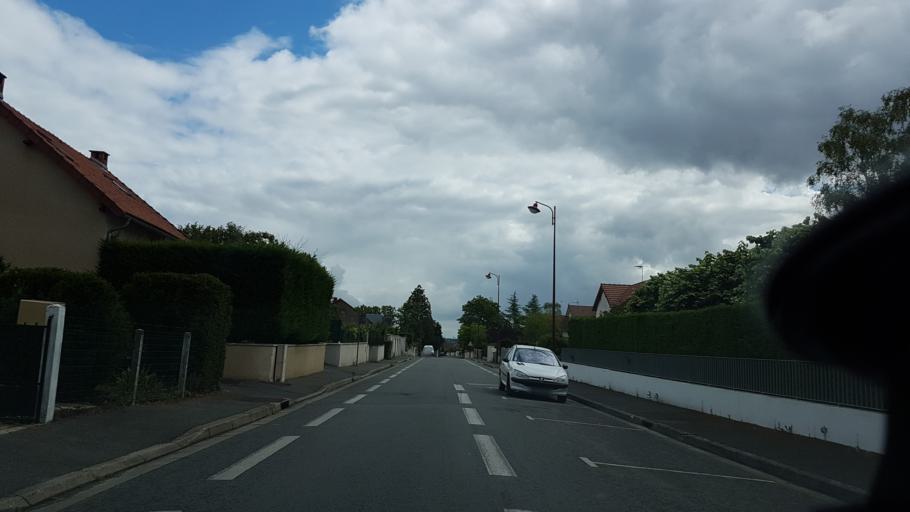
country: FR
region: Centre
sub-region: Departement du Cher
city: Saint-Doulchard
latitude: 47.1074
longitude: 2.3670
